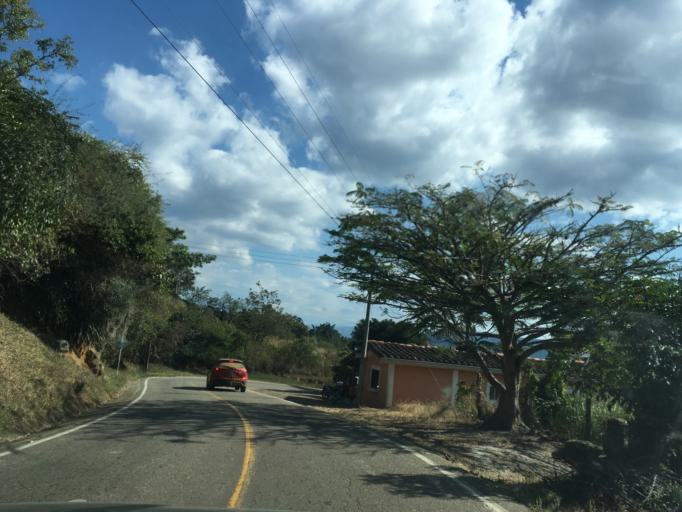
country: CO
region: Santander
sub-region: San Gil
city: San Gil
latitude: 6.5941
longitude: -73.1589
